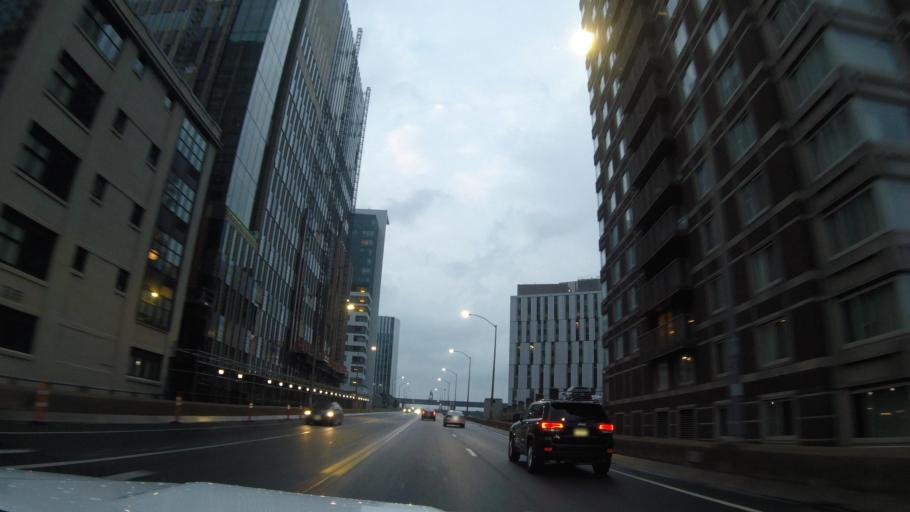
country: US
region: Massachusetts
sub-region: Suffolk County
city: Boston
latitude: 42.3700
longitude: -71.0726
